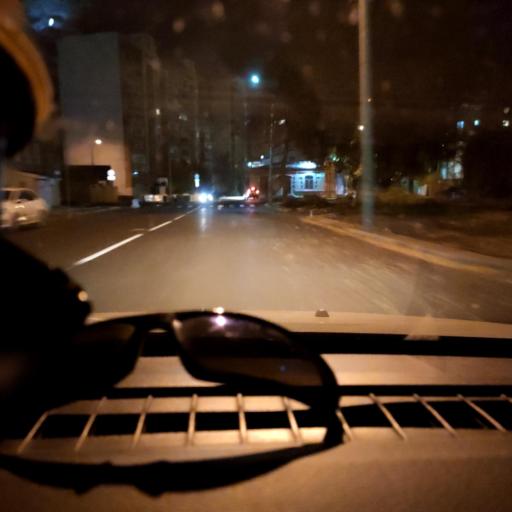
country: RU
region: Samara
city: Samara
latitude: 53.1870
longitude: 50.1114
